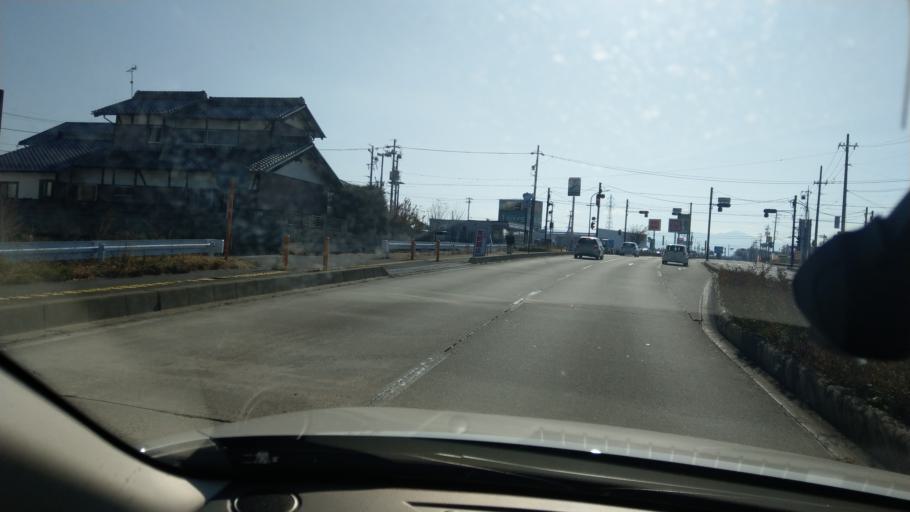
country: JP
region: Nagano
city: Komoro
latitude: 36.3002
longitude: 138.4670
